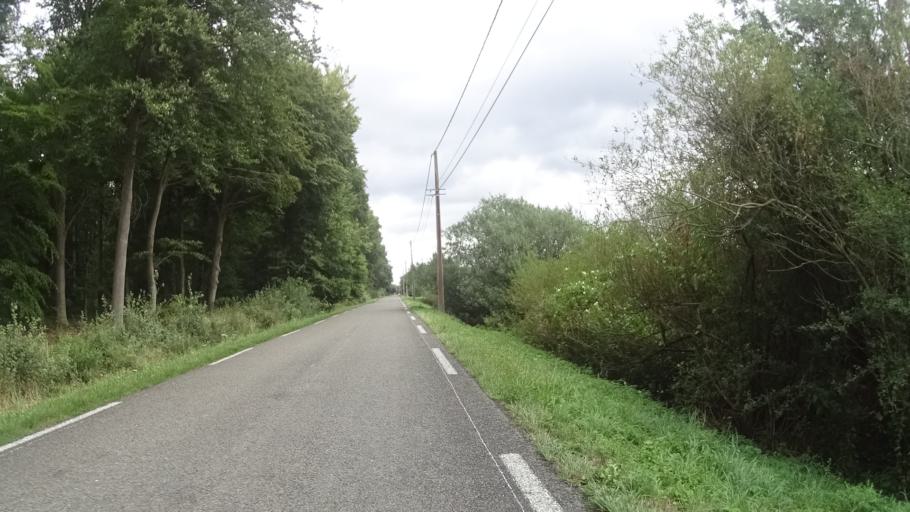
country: FR
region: Nord-Pas-de-Calais
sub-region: Departement du Nord
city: Maroilles
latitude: 50.1579
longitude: 3.7520
